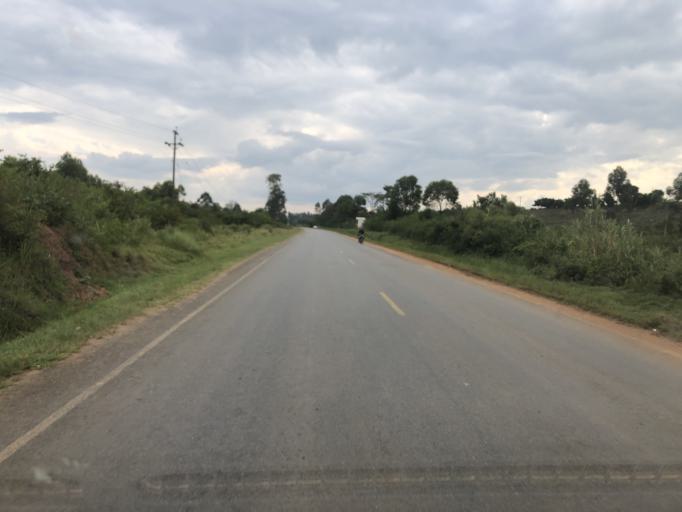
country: UG
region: Western Region
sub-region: Sheema District
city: Kibingo
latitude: -0.5794
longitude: 30.4247
